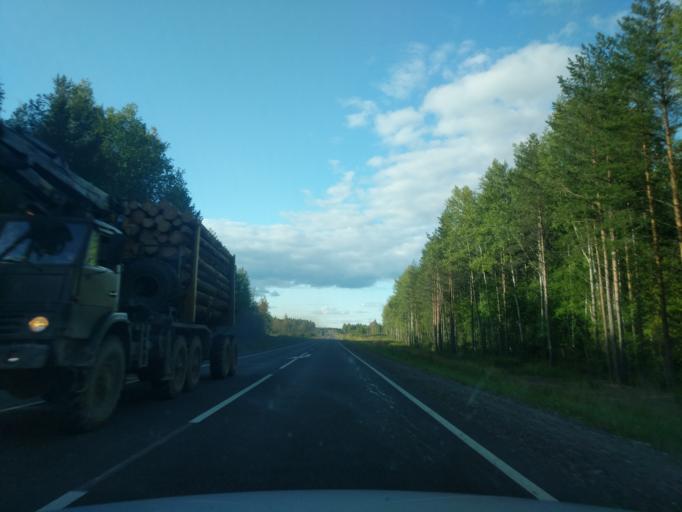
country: RU
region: Kostroma
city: Manturovo
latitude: 58.3206
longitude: 44.7184
